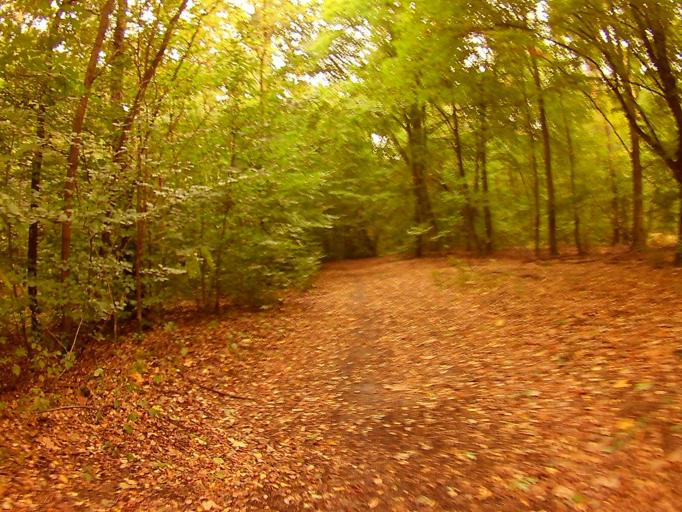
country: DE
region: Brandenburg
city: Zeuthen
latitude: 52.3979
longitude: 13.6203
